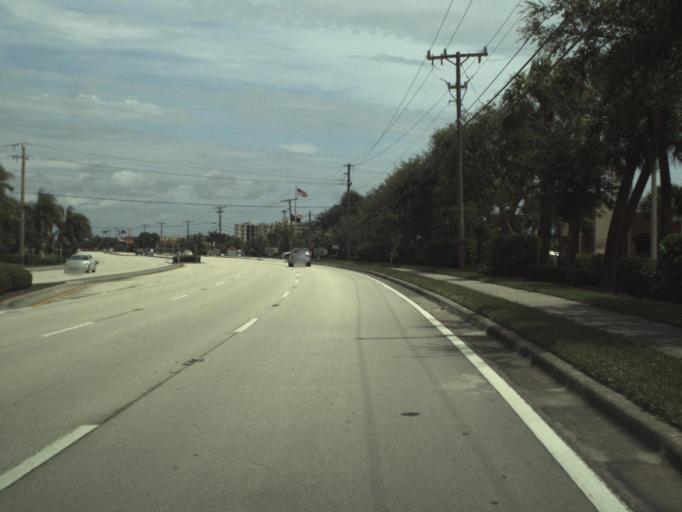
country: US
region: Florida
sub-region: Palm Beach County
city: Jupiter
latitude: 26.9613
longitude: -80.0845
